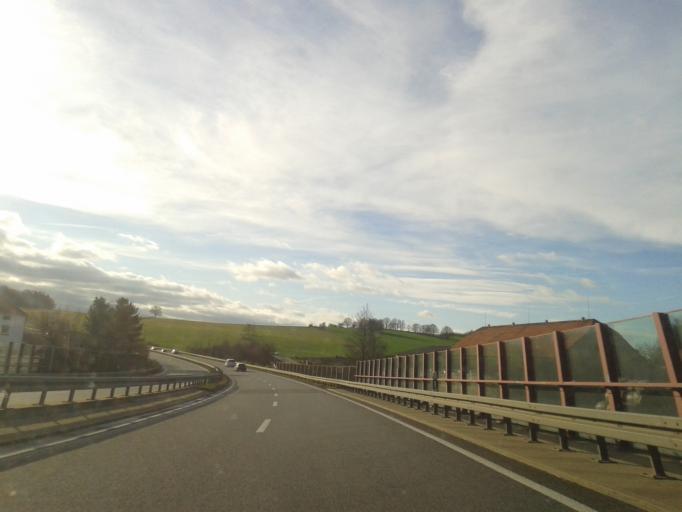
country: DE
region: Saxony
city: Lobau
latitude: 51.0992
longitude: 14.6417
